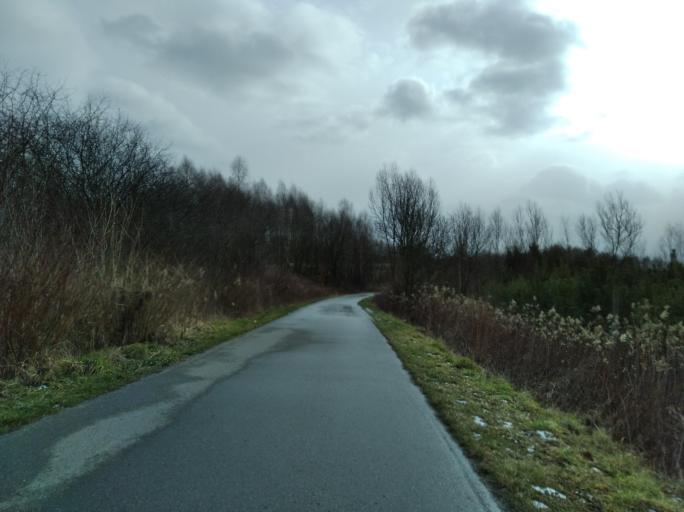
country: PL
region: Subcarpathian Voivodeship
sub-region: Powiat strzyzowski
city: Wysoka Strzyzowska
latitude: 49.8898
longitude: 21.7283
